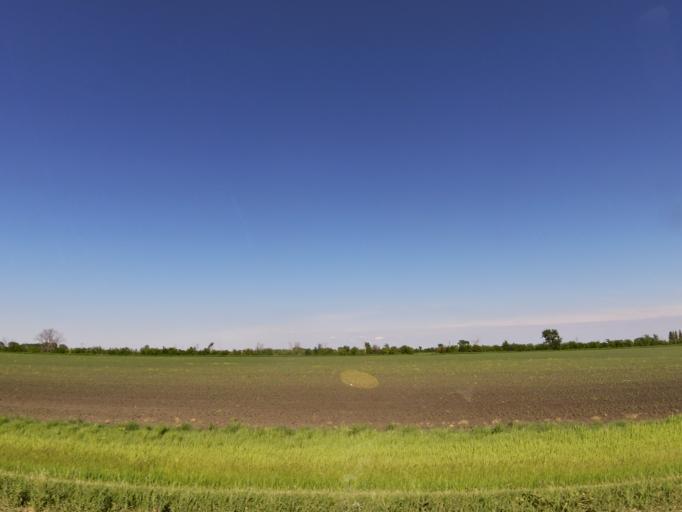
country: US
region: North Dakota
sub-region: Walsh County
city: Grafton
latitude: 48.3878
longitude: -97.2777
